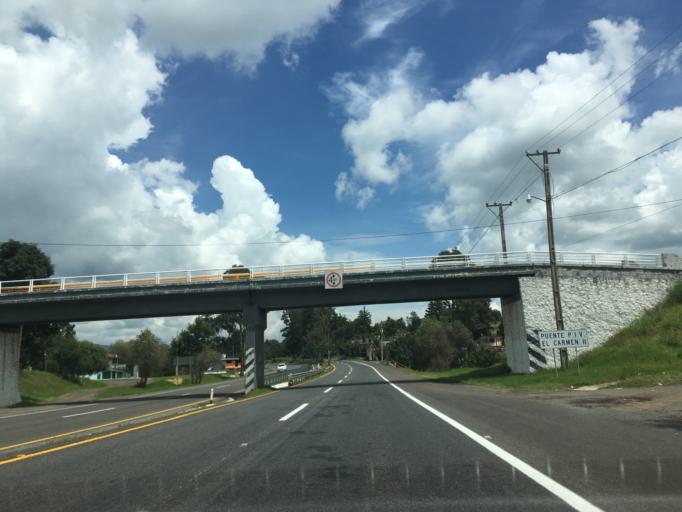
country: MX
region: Michoacan
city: Huiramba
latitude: 19.5404
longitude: -101.4598
